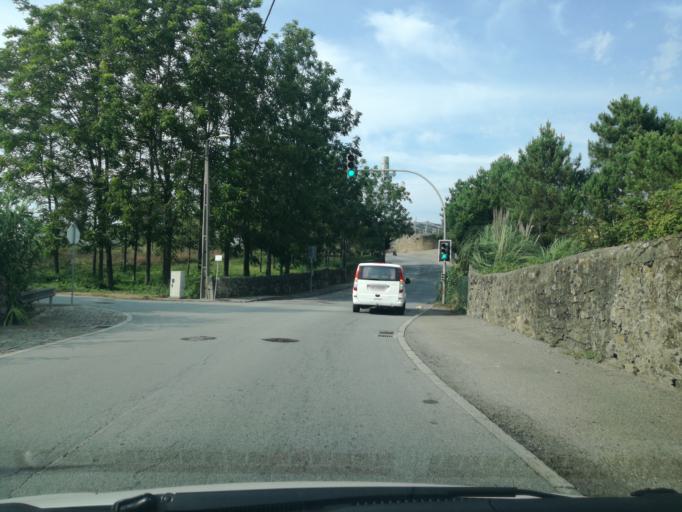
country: PT
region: Porto
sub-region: Vila Nova de Gaia
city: Arcozelo
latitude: 41.0599
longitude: -8.6279
